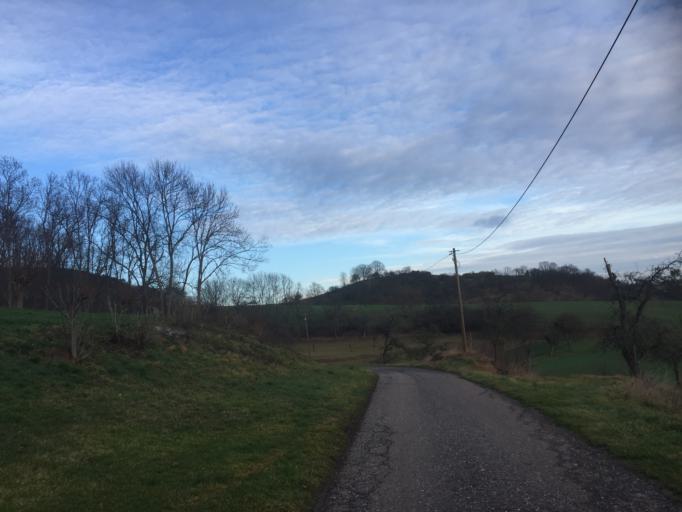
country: DE
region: Thuringia
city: Orlamunde
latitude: 50.7725
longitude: 11.4959
